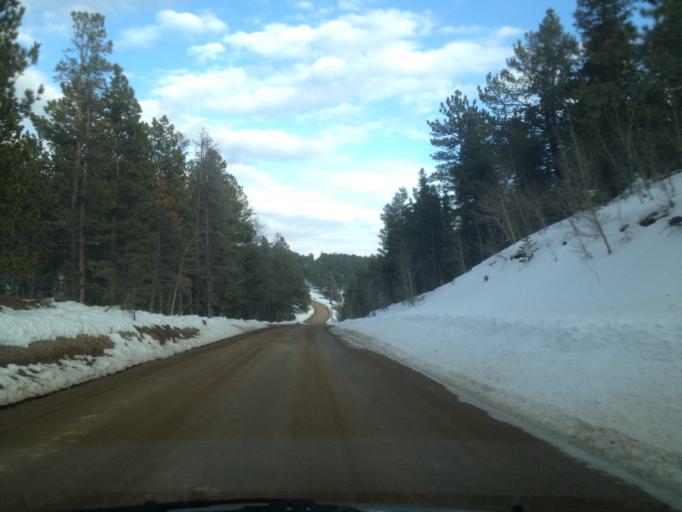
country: US
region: Colorado
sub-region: Boulder County
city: Nederland
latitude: 40.1260
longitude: -105.4688
